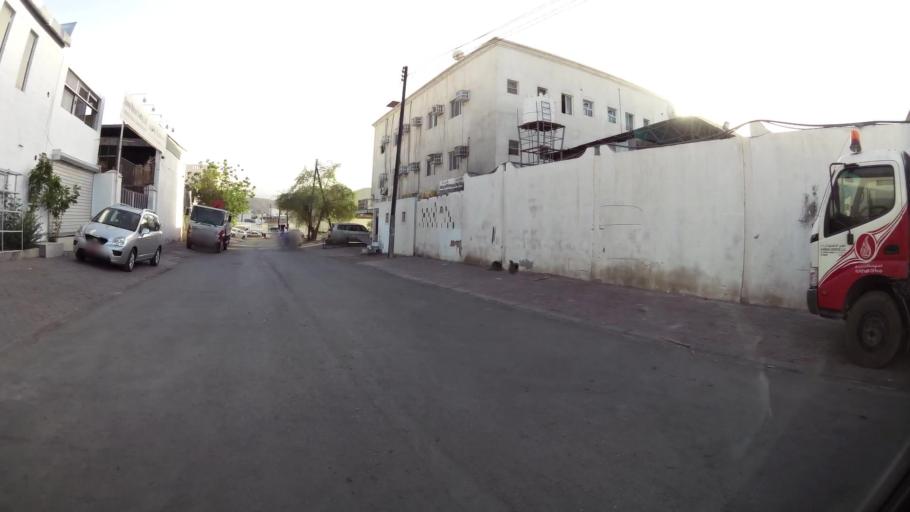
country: OM
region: Muhafazat Masqat
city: Muscat
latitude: 23.5880
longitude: 58.5576
